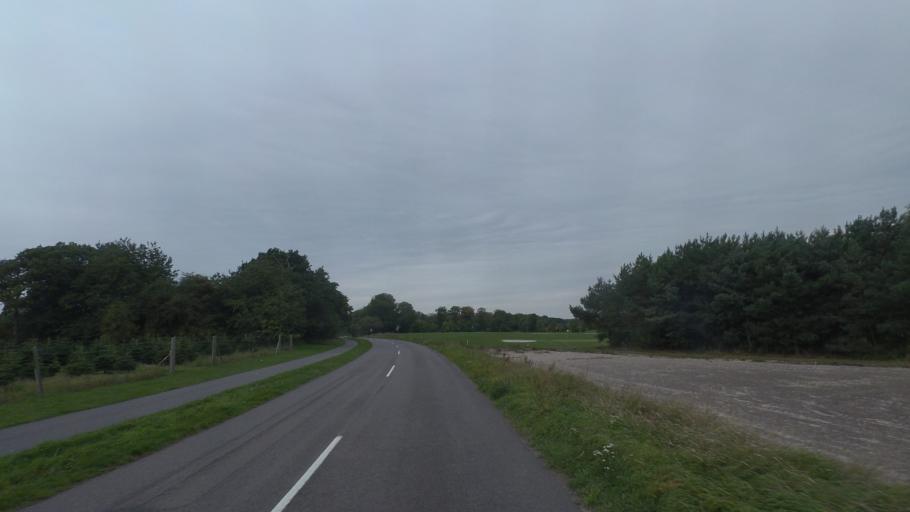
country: DK
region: Capital Region
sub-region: Bornholm Kommune
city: Nexo
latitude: 55.0036
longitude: 15.0353
